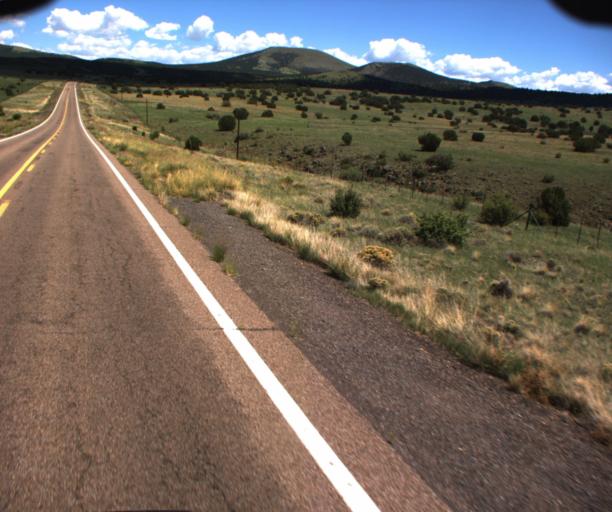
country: US
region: Arizona
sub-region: Navajo County
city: Pinetop-Lakeside
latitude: 34.2706
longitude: -109.6450
